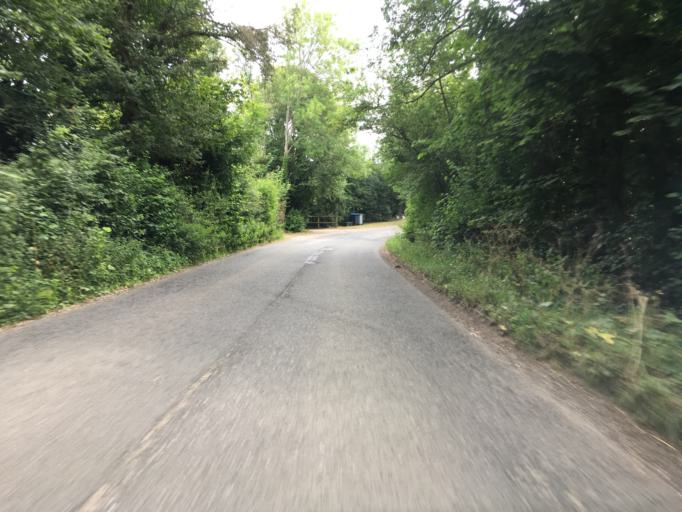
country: GB
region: England
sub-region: Oxfordshire
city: Charlbury
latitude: 51.8958
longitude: -1.5031
